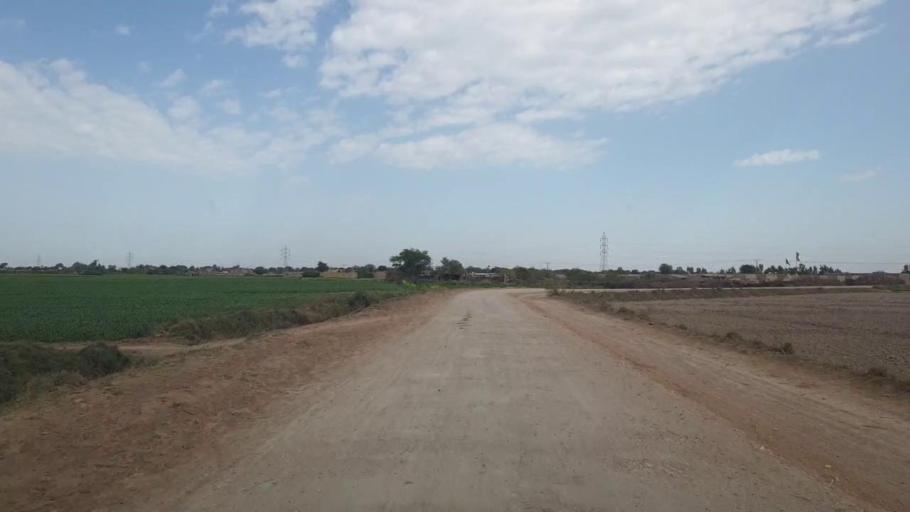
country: PK
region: Sindh
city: Sakrand
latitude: 26.0108
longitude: 68.3480
